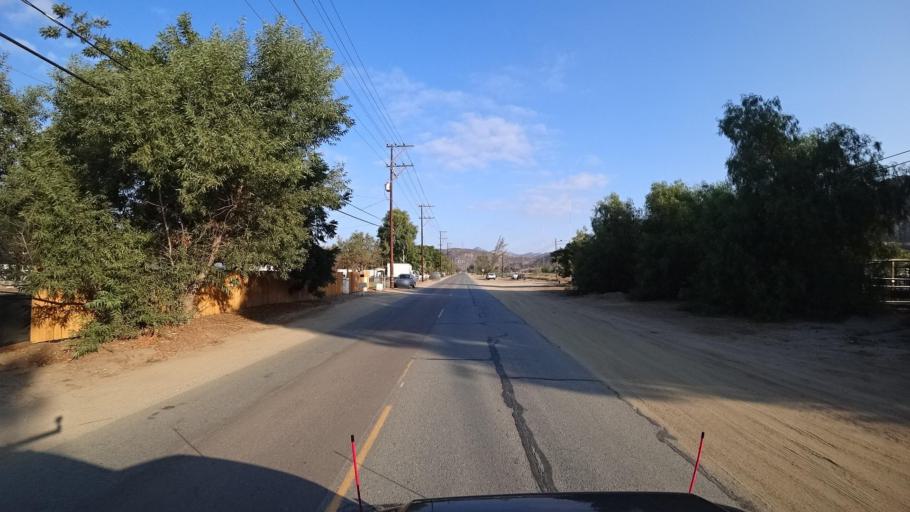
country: US
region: California
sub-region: San Diego County
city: Eucalyptus Hills
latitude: 32.8912
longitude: -116.9270
